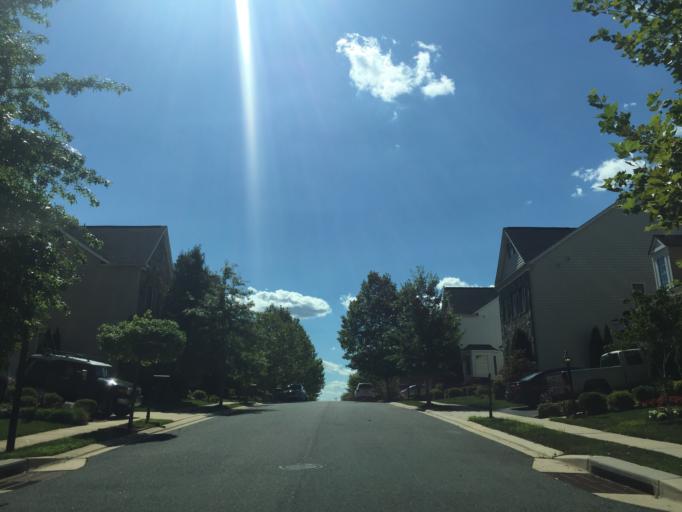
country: US
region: Maryland
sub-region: Baltimore County
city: White Marsh
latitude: 39.3878
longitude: -76.4337
